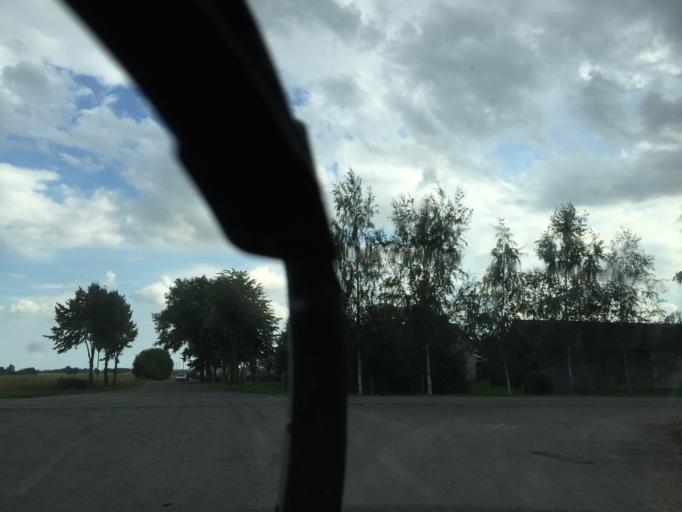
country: LV
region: Dobeles Rajons
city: Dobele
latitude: 56.6200
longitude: 23.3960
